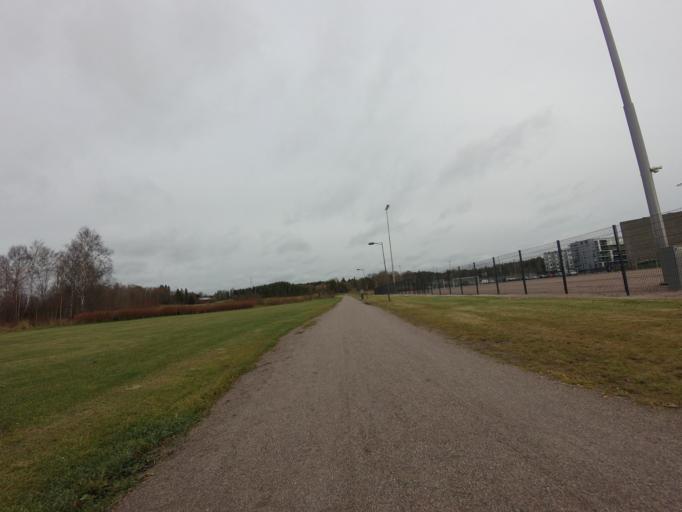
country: FI
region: Uusimaa
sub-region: Helsinki
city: Kauniainen
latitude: 60.1912
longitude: 24.7364
